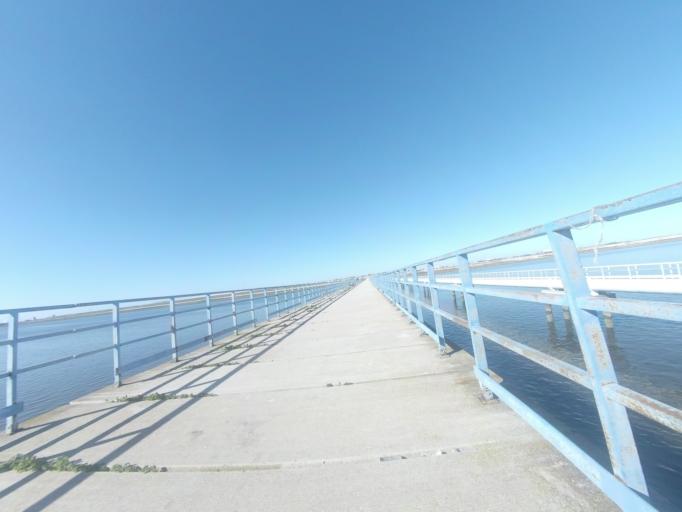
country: ES
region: Andalusia
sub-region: Provincia de Huelva
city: Palos de la Frontera
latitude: 37.2483
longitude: -6.8968
